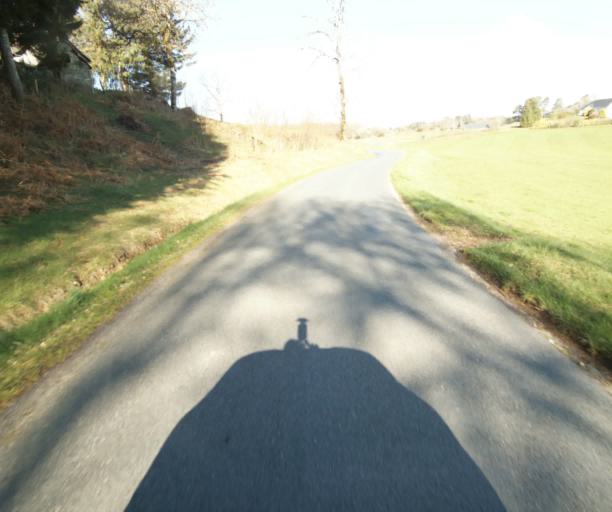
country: FR
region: Limousin
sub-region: Departement de la Correze
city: Correze
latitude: 45.2746
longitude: 1.8856
